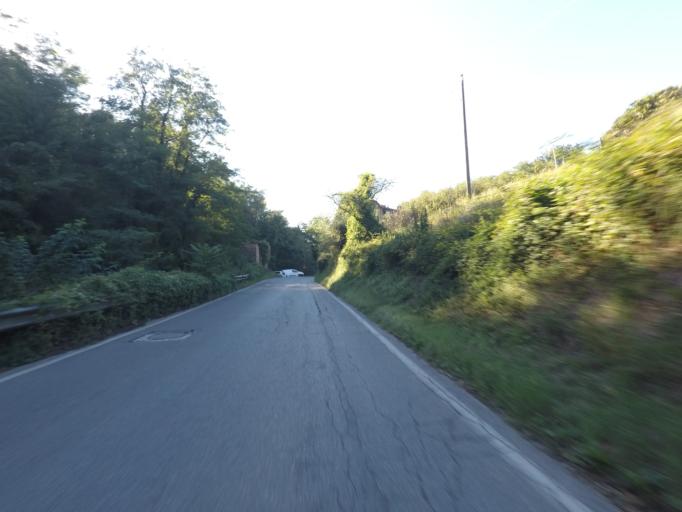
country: IT
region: Tuscany
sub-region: Provincia di Lucca
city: Stiava
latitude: 43.9064
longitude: 10.3499
